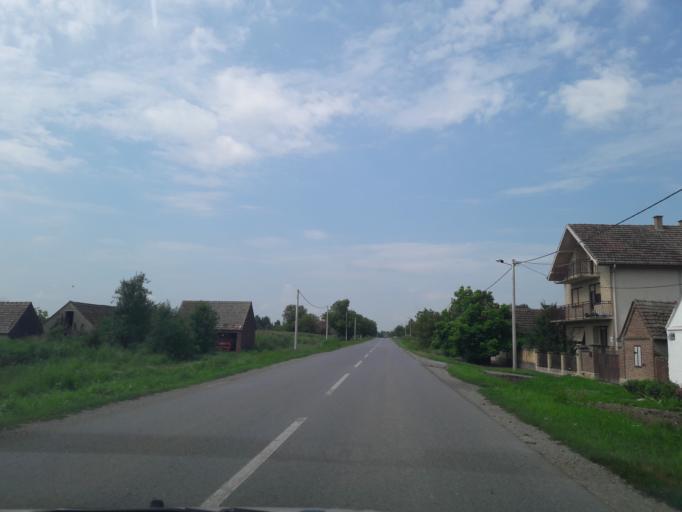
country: HR
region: Osjecko-Baranjska
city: Gorjani
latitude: 45.4701
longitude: 18.3434
